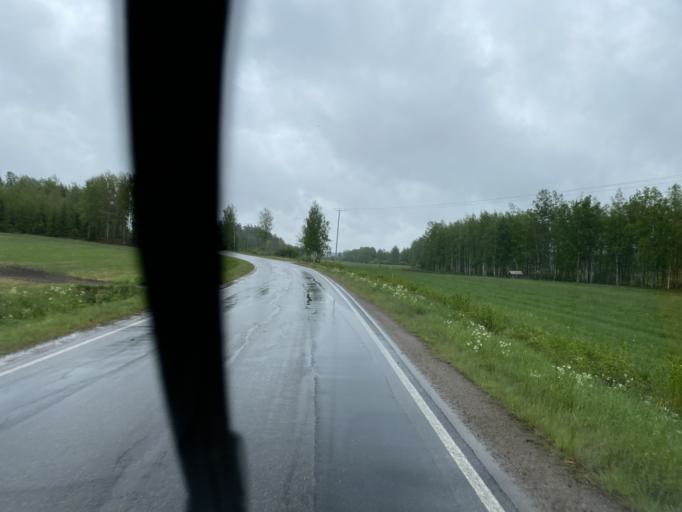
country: FI
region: Haeme
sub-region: Forssa
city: Humppila
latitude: 61.0402
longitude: 23.4104
